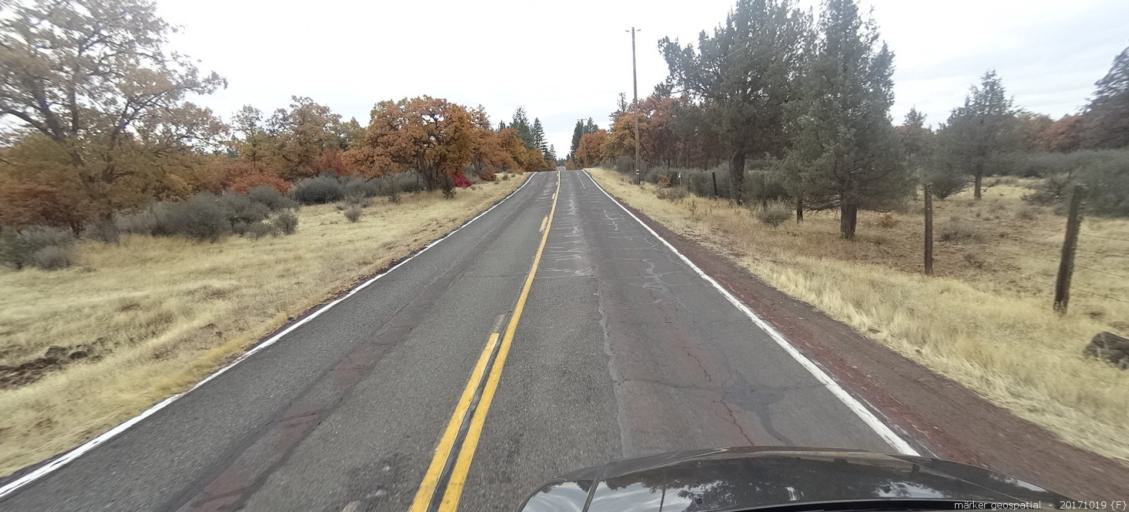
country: US
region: California
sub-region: Shasta County
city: Burney
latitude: 41.0969
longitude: -121.3206
